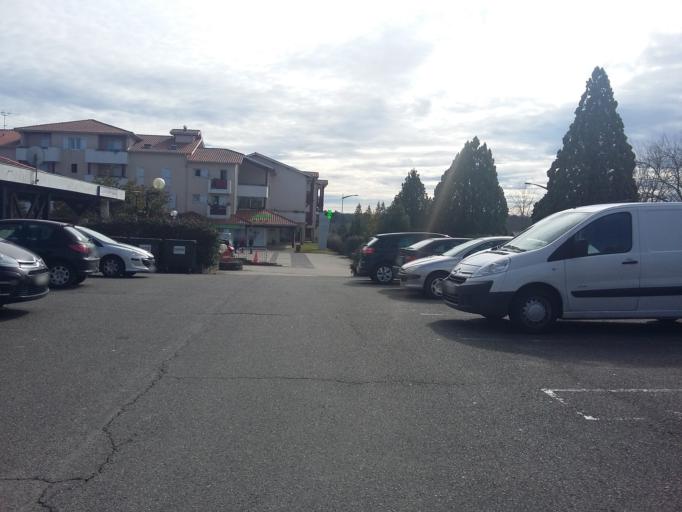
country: FR
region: Aquitaine
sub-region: Departement des Landes
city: Saint-Martin-de-Seignanx
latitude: 43.5419
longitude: -1.3872
